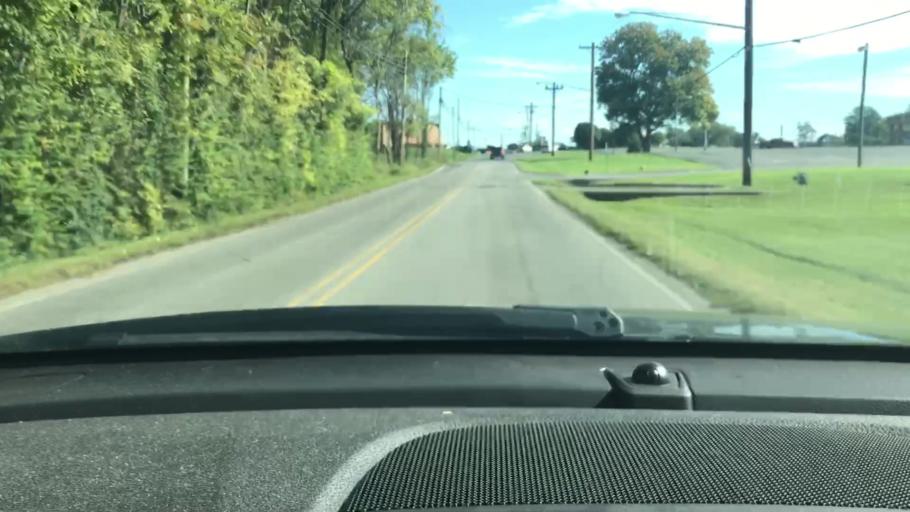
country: US
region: Tennessee
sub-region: Sumner County
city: Hendersonville
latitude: 36.3015
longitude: -86.6352
